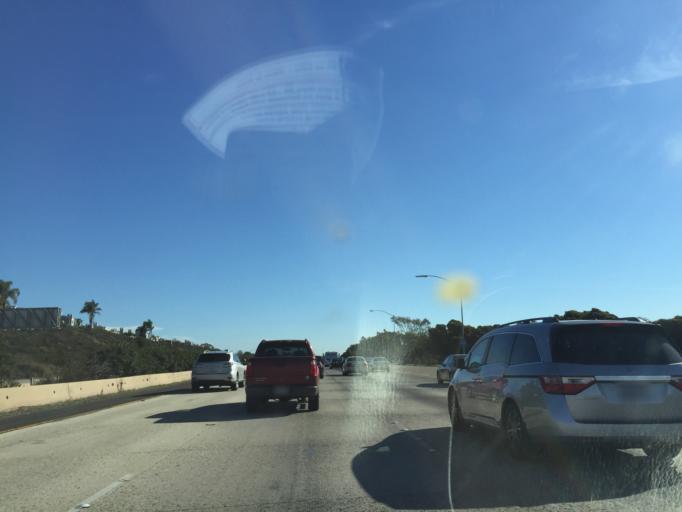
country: US
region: California
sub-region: San Diego County
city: Encinitas
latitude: 33.1008
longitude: -117.3091
